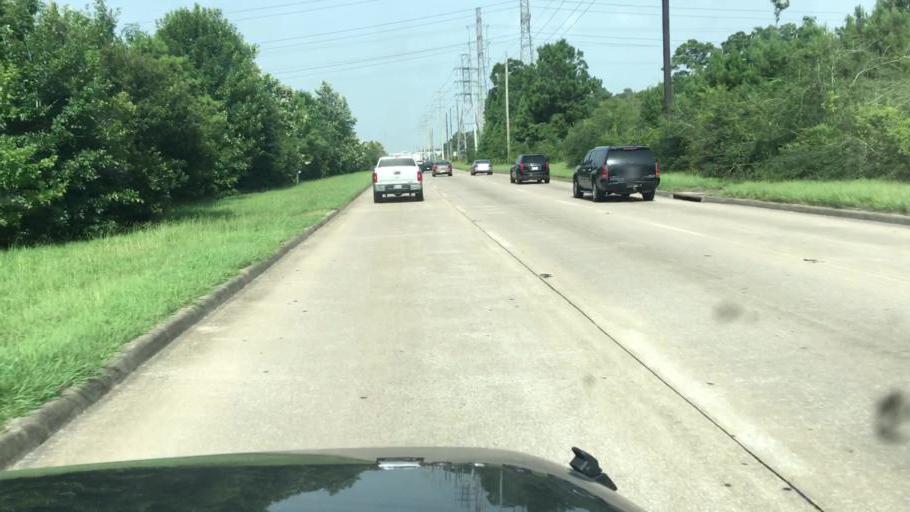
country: US
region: Texas
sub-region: Harris County
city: Humble
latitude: 29.9338
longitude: -95.2210
